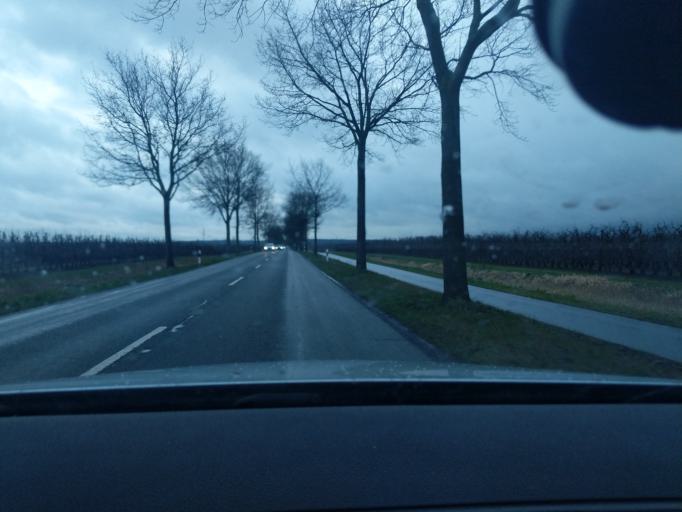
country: DE
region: Lower Saxony
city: Jork
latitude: 53.5122
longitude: 9.6670
